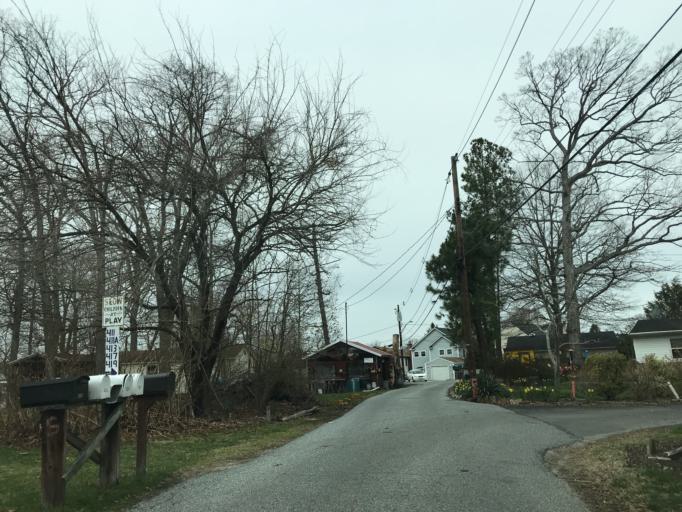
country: US
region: Maryland
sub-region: Baltimore County
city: Middle River
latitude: 39.3007
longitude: -76.4275
